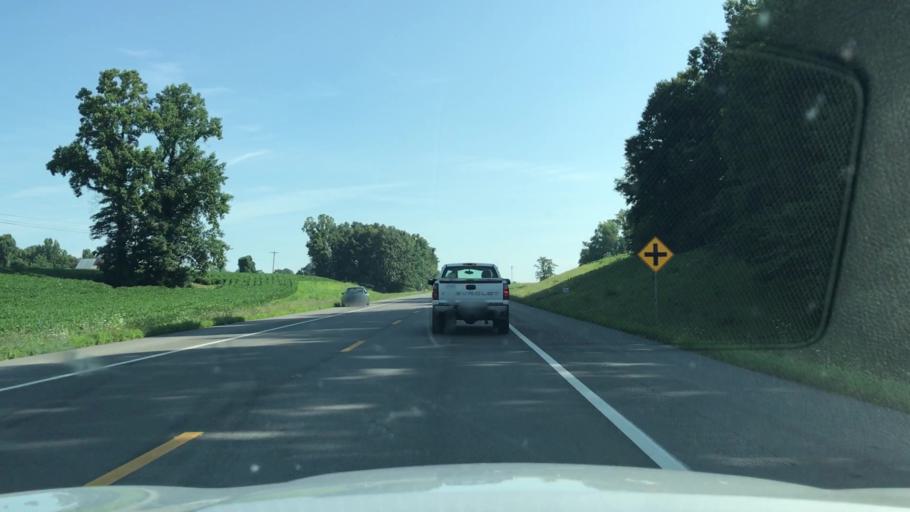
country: US
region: Tennessee
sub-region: Pickett County
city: Byrdstown
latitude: 36.4925
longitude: -85.1810
